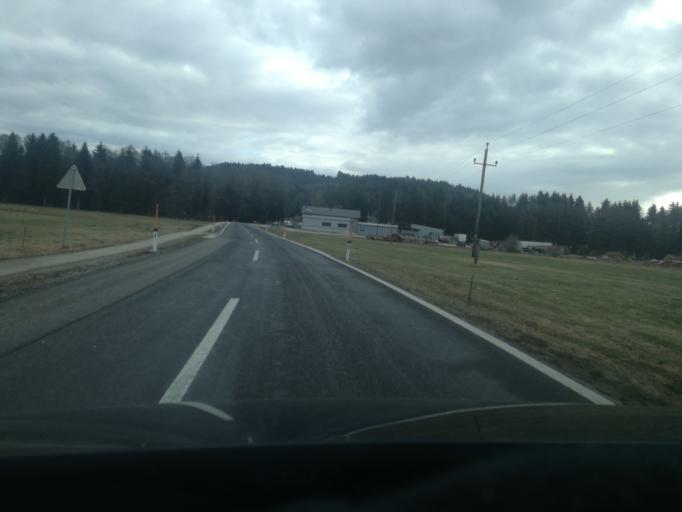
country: AT
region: Upper Austria
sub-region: Politischer Bezirk Vocklabruck
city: Pfaffing
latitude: 48.0376
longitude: 13.4939
